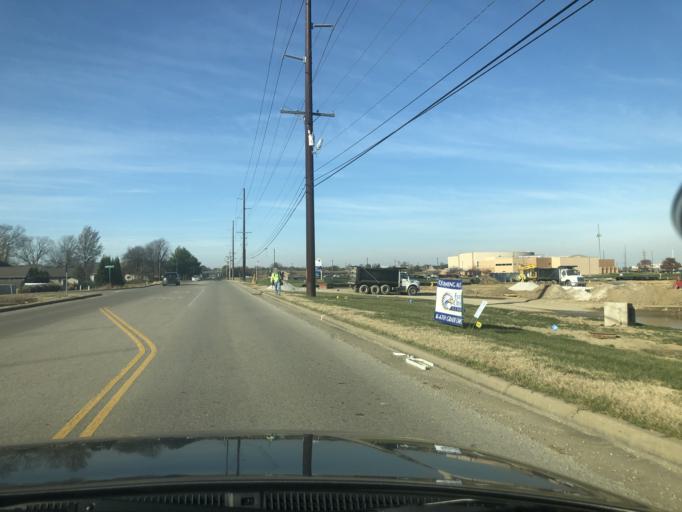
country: US
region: Indiana
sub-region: Warrick County
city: Newburgh
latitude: 37.9695
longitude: -87.4431
